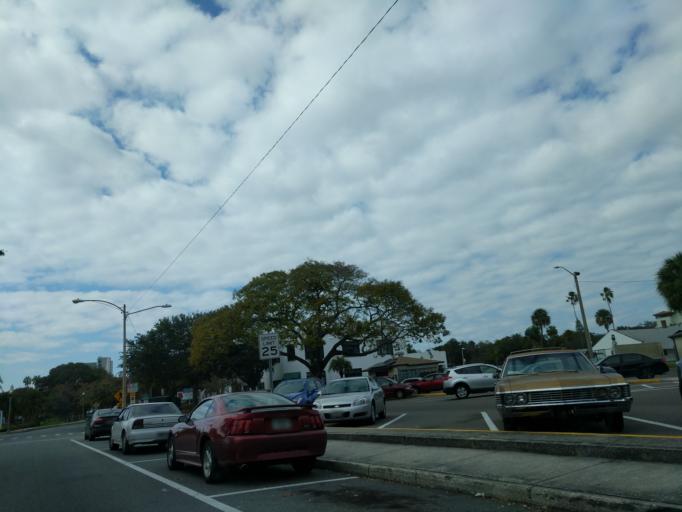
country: US
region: Florida
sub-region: Pinellas County
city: Saint Petersburg
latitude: 27.7752
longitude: -82.6404
